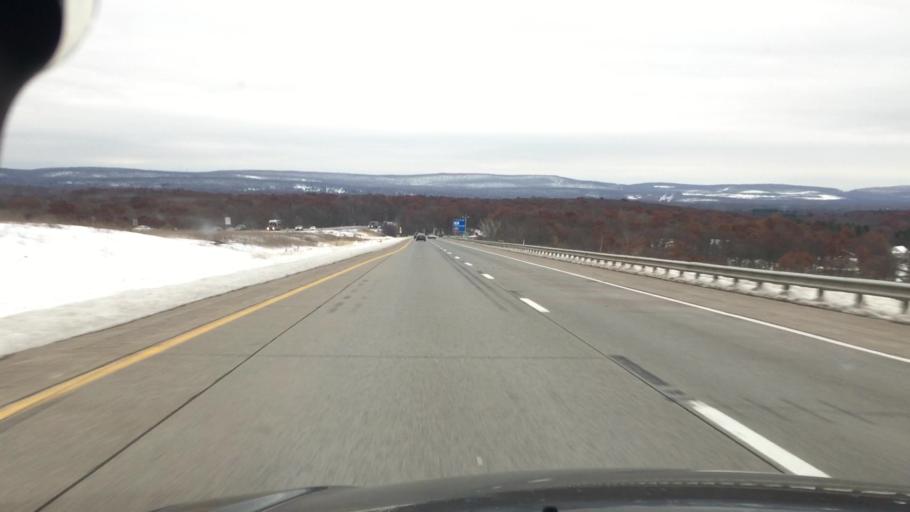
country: US
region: Pennsylvania
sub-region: Luzerne County
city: Nanticoke
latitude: 41.1669
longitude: -75.9567
